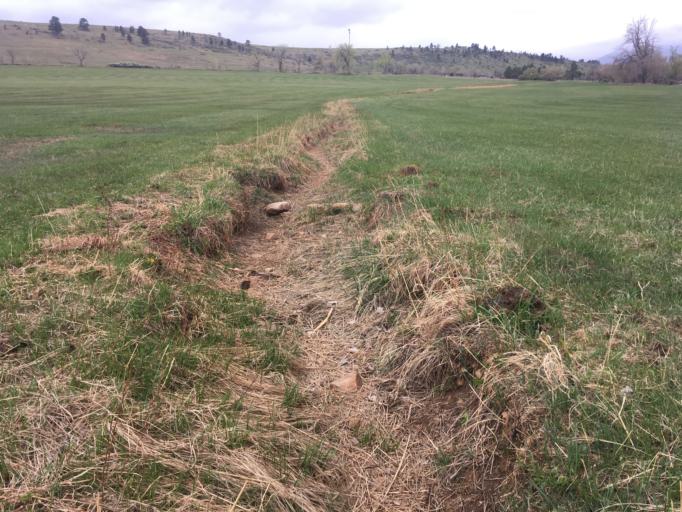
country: US
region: Colorado
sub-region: Boulder County
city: Superior
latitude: 39.9693
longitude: -105.2111
